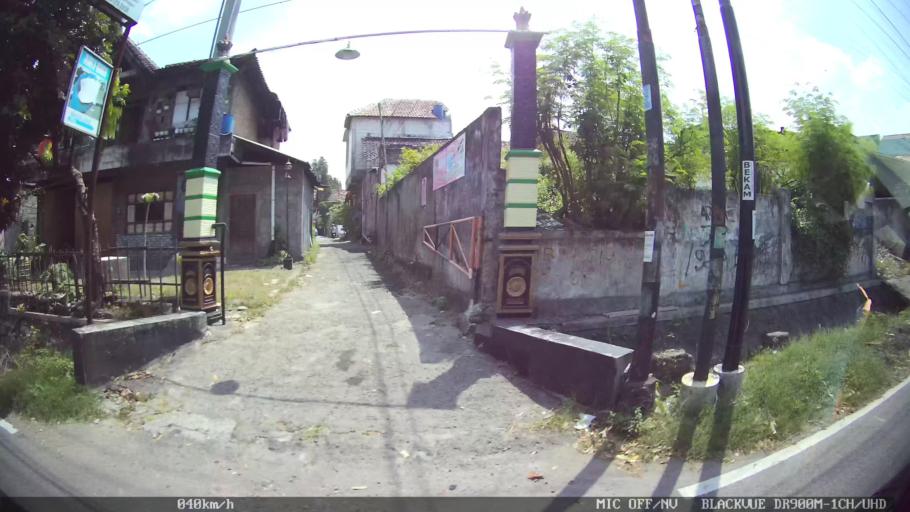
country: ID
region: Daerah Istimewa Yogyakarta
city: Yogyakarta
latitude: -7.8246
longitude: 110.4095
